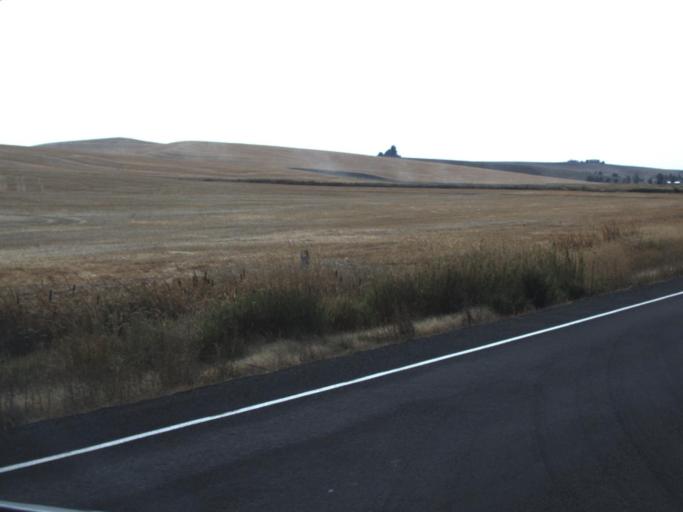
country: US
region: Washington
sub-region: Whitman County
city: Pullman
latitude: 46.8808
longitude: -117.1257
